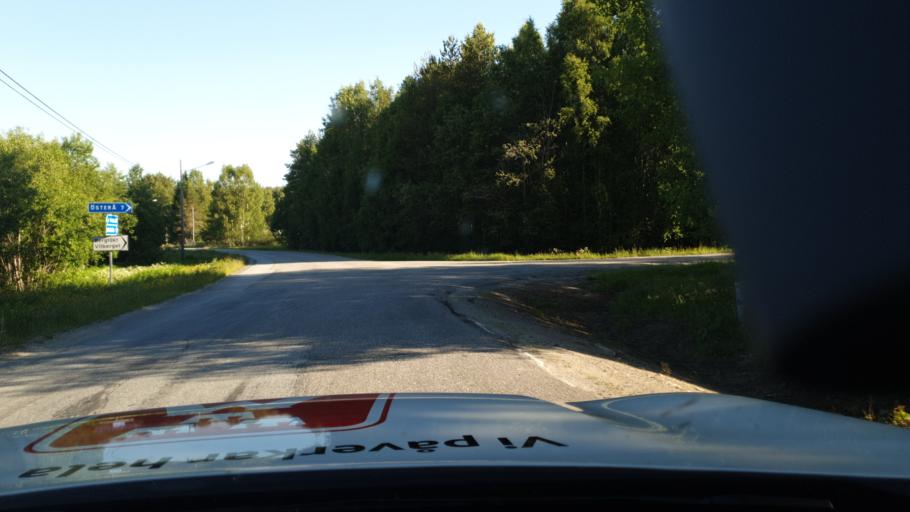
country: SE
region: Vaesterbotten
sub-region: Vannas Kommun
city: Vannasby
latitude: 64.0736
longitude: 20.0652
